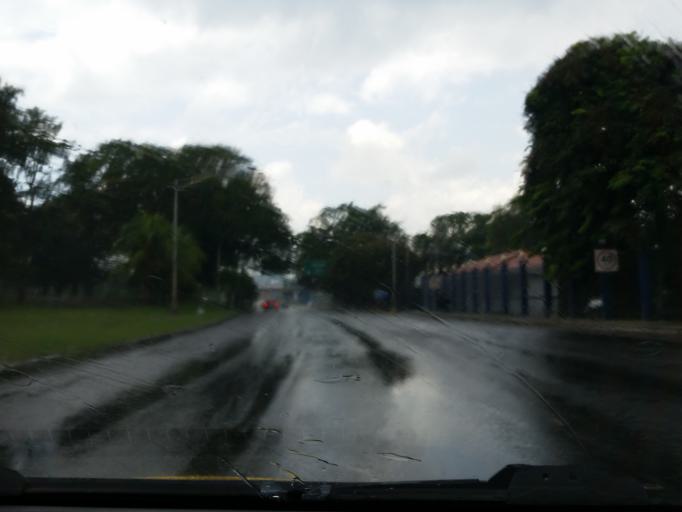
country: PA
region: Panama
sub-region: Distrito de Panama
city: Ancon
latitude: 8.9659
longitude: -79.5514
